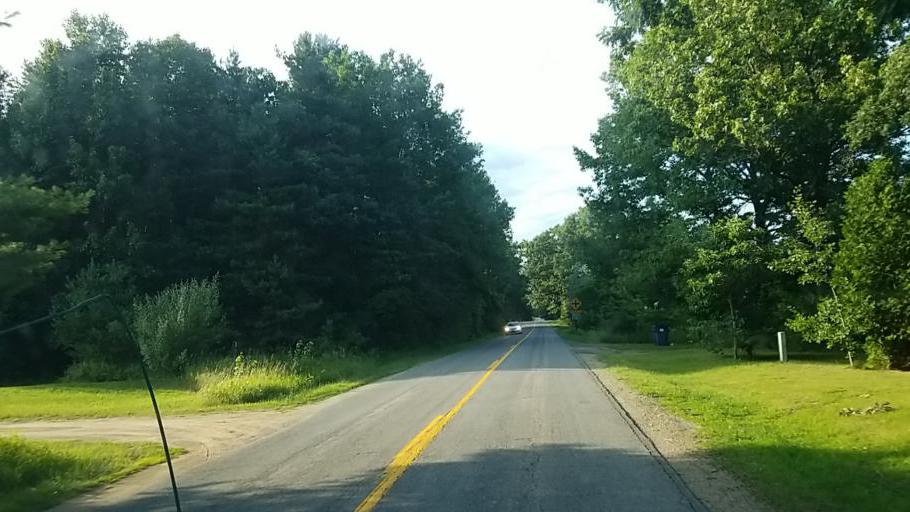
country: US
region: Michigan
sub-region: Montcalm County
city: Greenville
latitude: 43.2700
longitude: -85.3622
